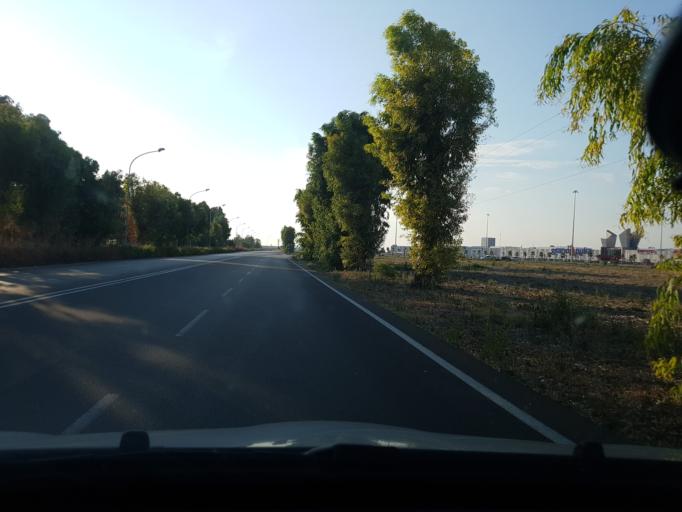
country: IT
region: Apulia
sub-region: Provincia di Foggia
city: Carapelle
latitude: 41.4118
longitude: 15.6524
